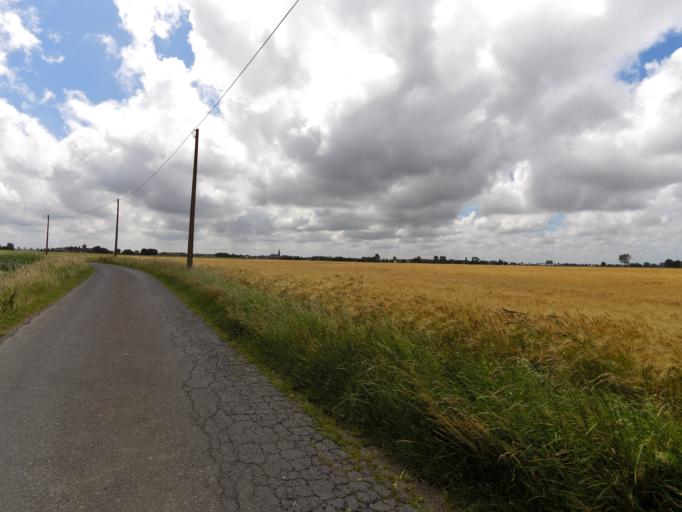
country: BE
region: Flanders
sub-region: Provincie West-Vlaanderen
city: Gistel
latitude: 51.1468
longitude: 2.9249
